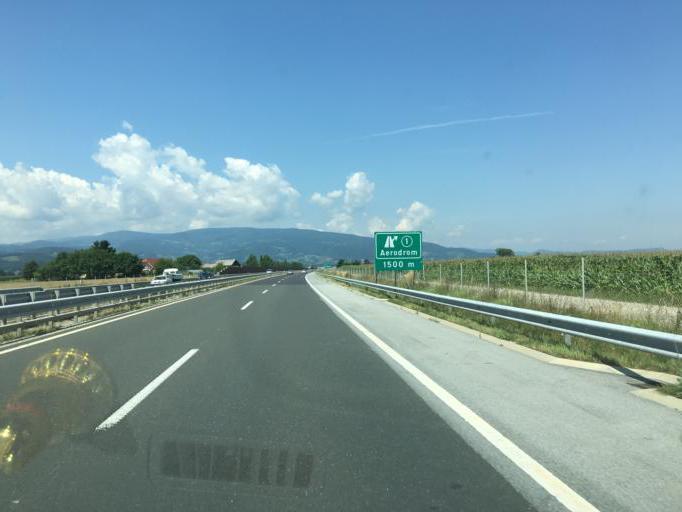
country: SI
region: Race-Fram
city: Race
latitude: 46.4634
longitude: 15.6971
